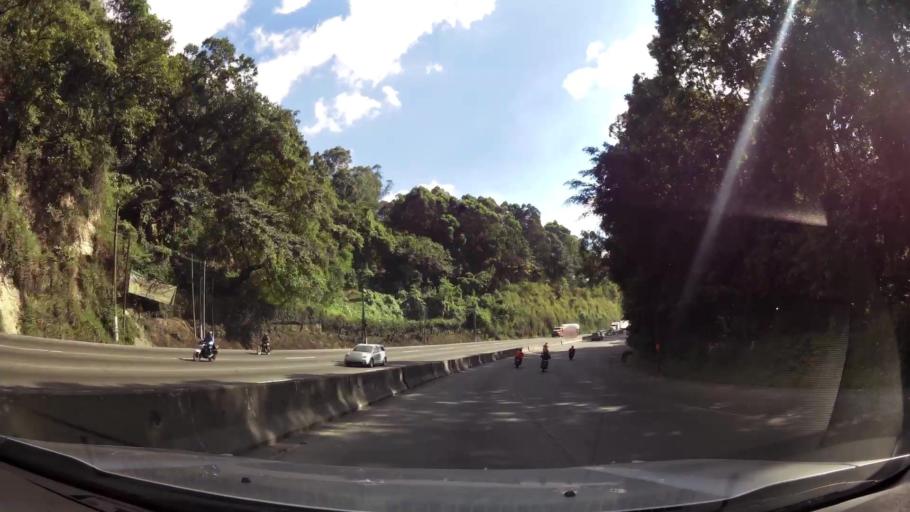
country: GT
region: Guatemala
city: Villa Nueva
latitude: 14.5576
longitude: -90.5760
